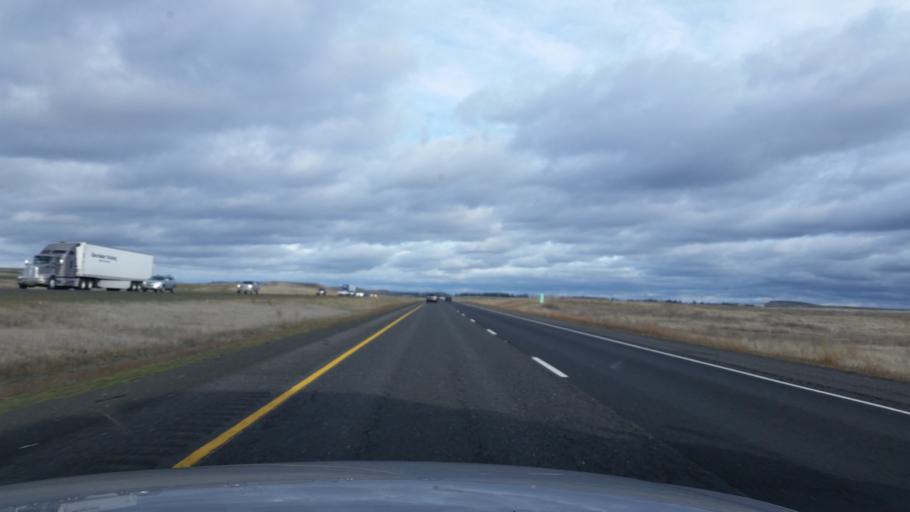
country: US
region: Washington
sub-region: Spokane County
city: Medical Lake
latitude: 47.3299
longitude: -117.9255
